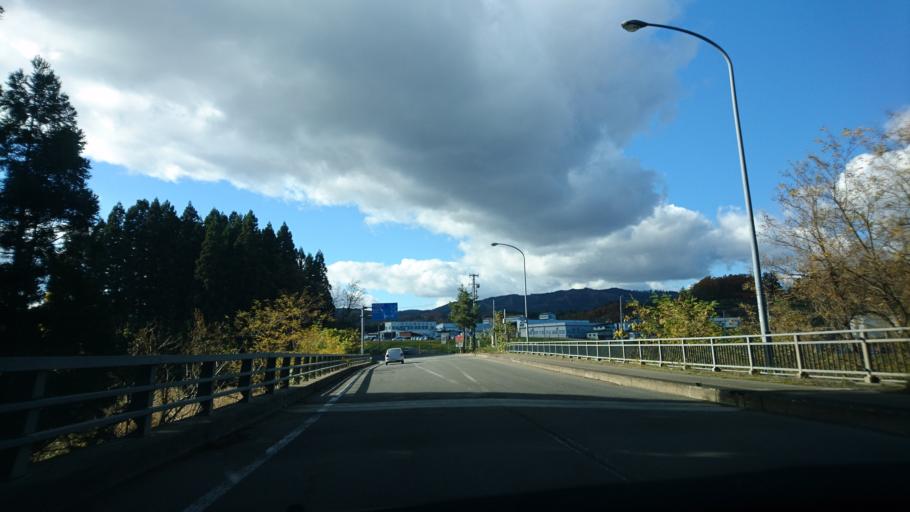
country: JP
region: Akita
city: Yuzawa
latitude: 39.2763
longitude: 140.3989
